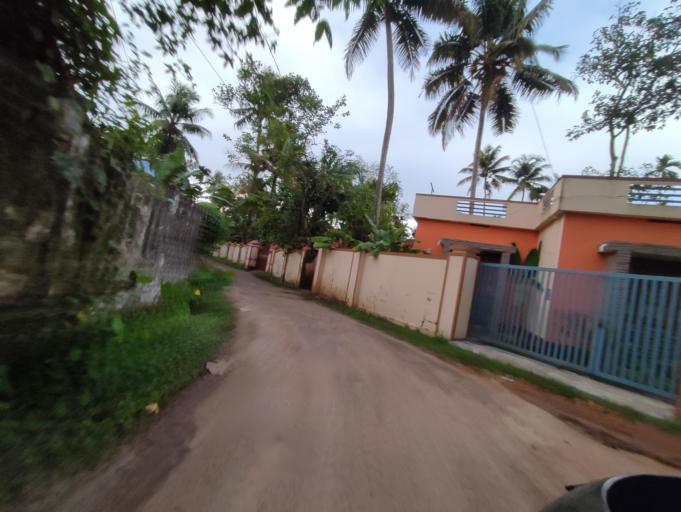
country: IN
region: Kerala
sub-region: Alappuzha
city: Vayalar
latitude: 9.6933
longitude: 76.3348
